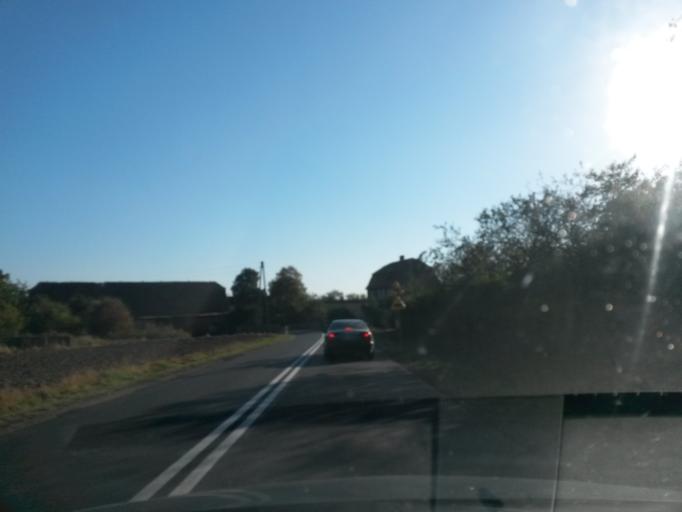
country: PL
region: Lower Silesian Voivodeship
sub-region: Powiat sredzki
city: Udanin
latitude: 51.0197
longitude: 16.4015
